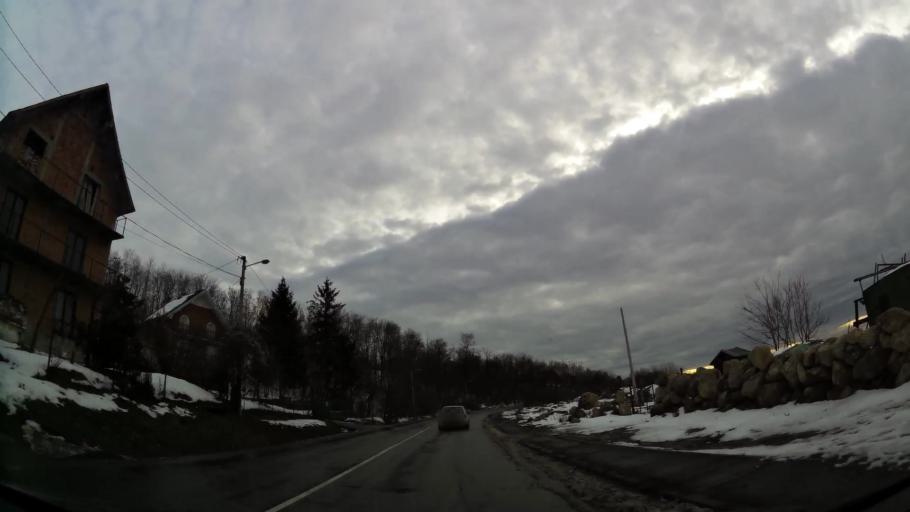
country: RS
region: Central Serbia
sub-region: Belgrade
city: Vozdovac
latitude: 44.7255
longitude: 20.4983
